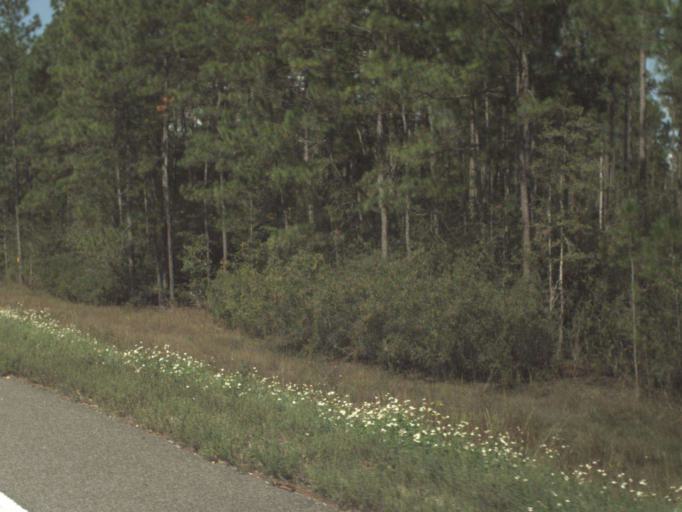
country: US
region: Florida
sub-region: Walton County
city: Freeport
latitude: 30.4591
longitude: -85.9226
